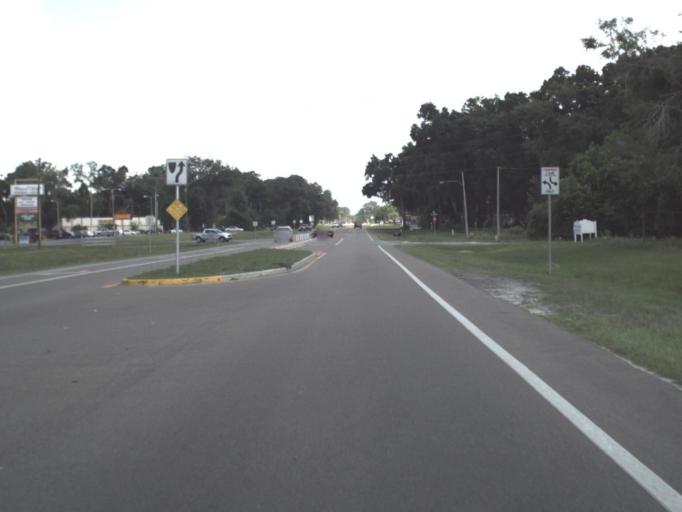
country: US
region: Florida
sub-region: Alachua County
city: High Springs
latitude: 29.8420
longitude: -82.6047
